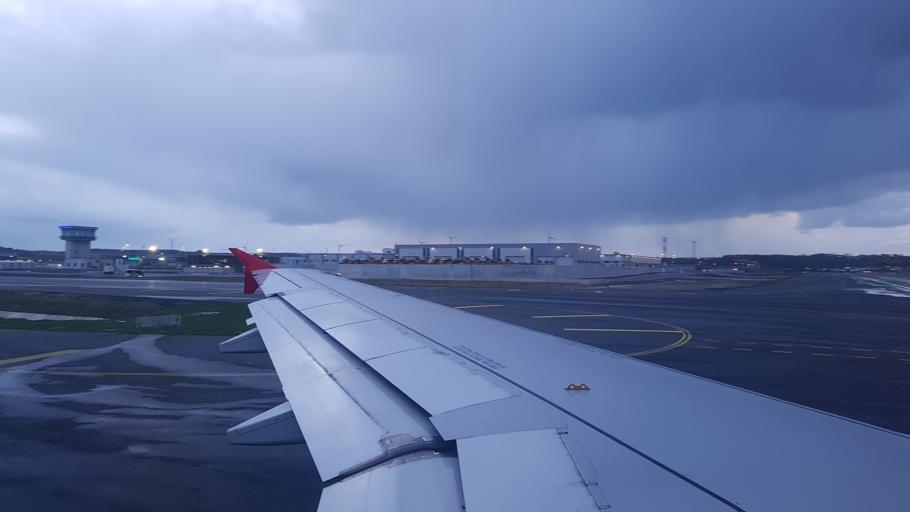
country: TR
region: Istanbul
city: Durusu
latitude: 41.2650
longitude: 28.7228
